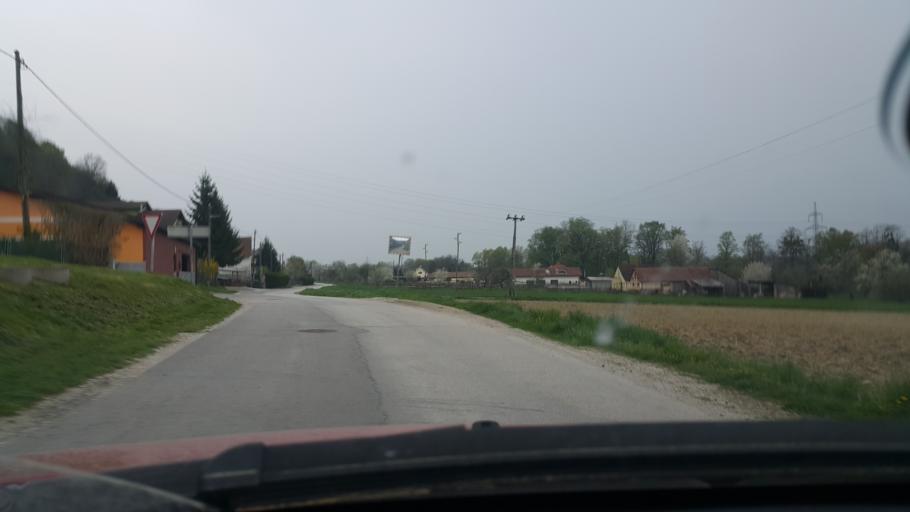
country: SI
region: Duplek
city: Zgornji Duplek
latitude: 46.5219
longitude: 15.7166
